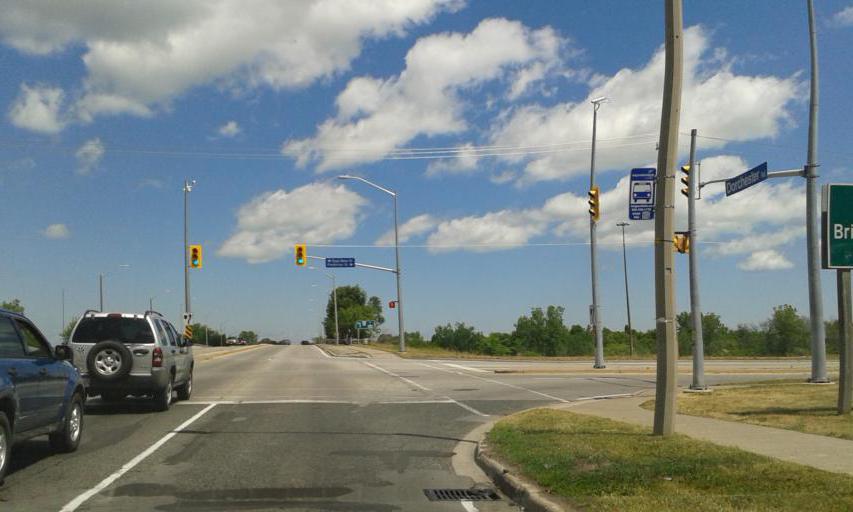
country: CA
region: Ontario
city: Niagara Falls
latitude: 43.0938
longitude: -79.1106
